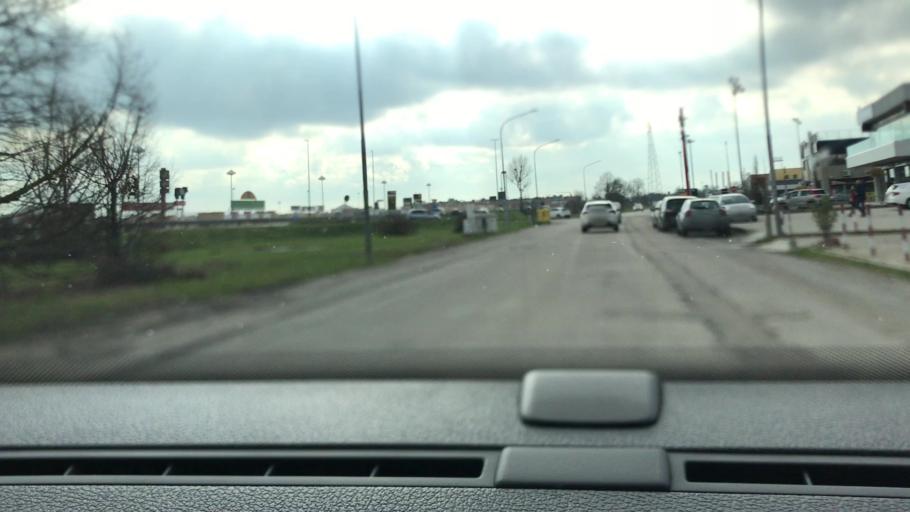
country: IT
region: Veneto
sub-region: Provincia di Rovigo
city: Grignano Polesine
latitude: 45.0347
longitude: 11.7783
